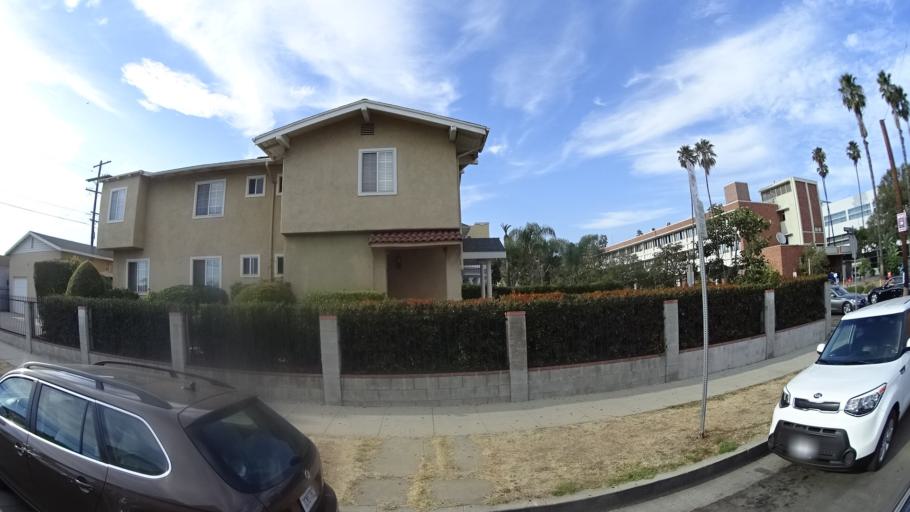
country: US
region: California
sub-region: Los Angeles County
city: Silver Lake
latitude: 34.0858
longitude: -118.2952
